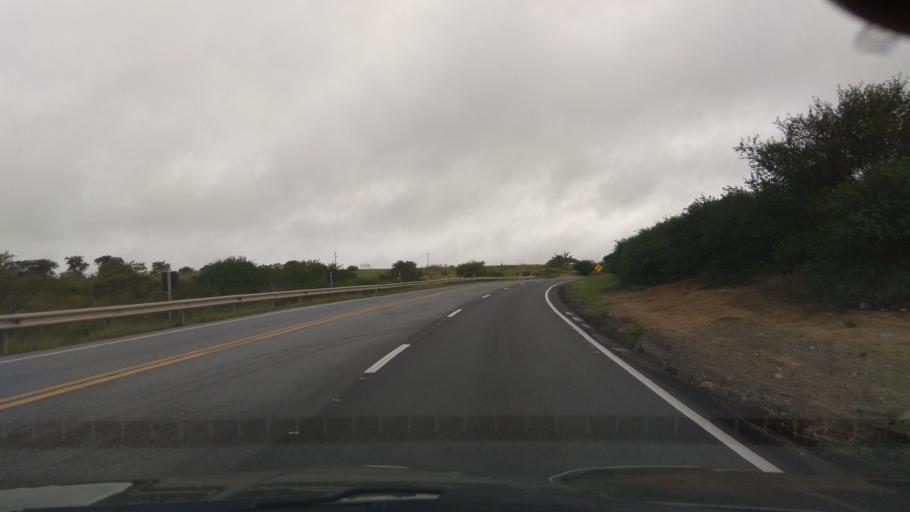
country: BR
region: Bahia
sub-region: Santa Ines
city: Santa Ines
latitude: -13.0597
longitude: -39.9568
